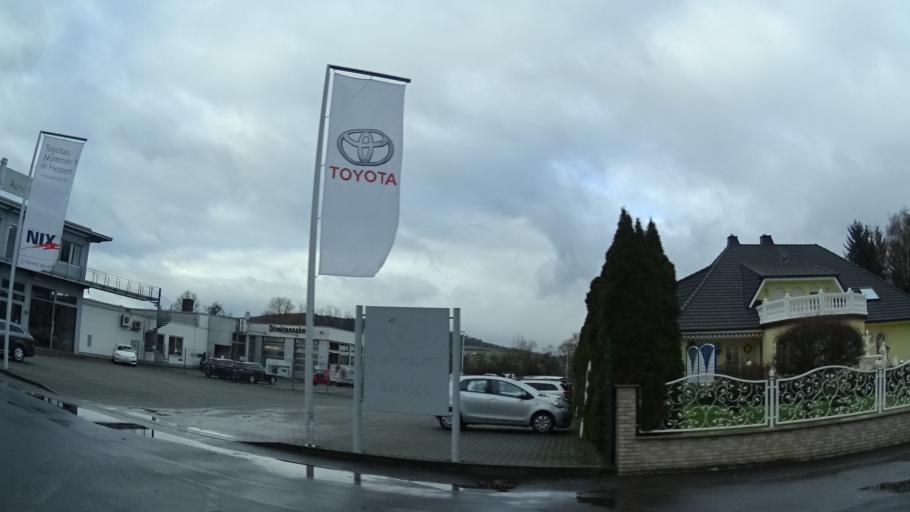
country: DE
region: Hesse
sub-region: Regierungsbezirk Darmstadt
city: Wachtersbach
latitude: 50.2515
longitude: 9.3142
